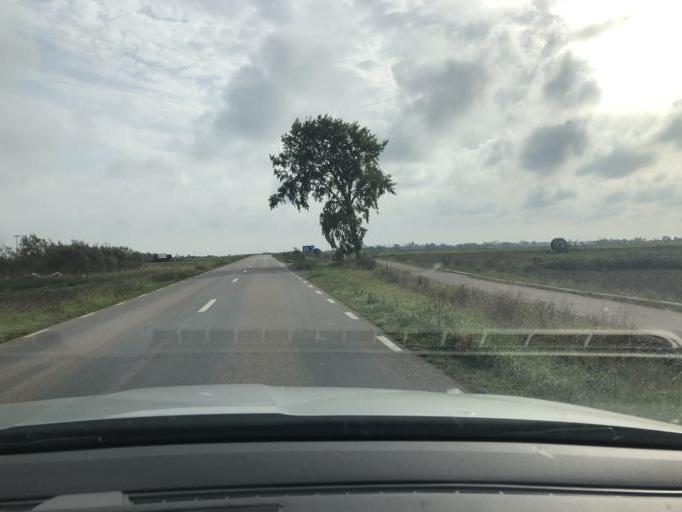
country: SE
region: Kalmar
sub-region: Morbylanga Kommun
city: Moerbylanga
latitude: 56.2967
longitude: 16.4092
